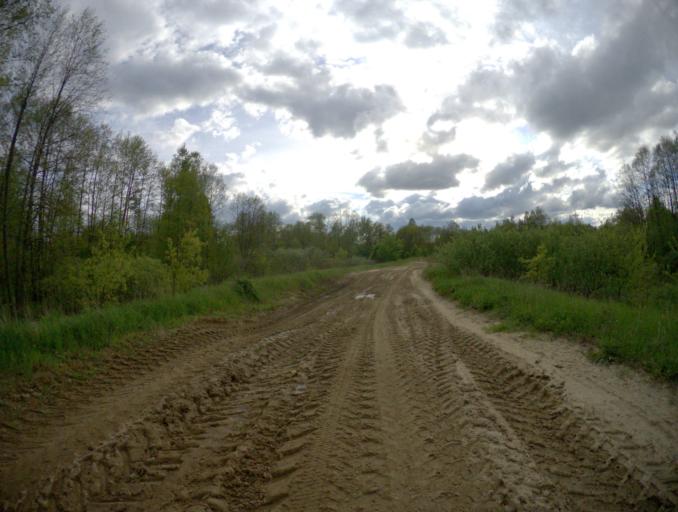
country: RU
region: Rjazan
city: Gus'-Zheleznyy
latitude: 55.1330
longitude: 41.1066
